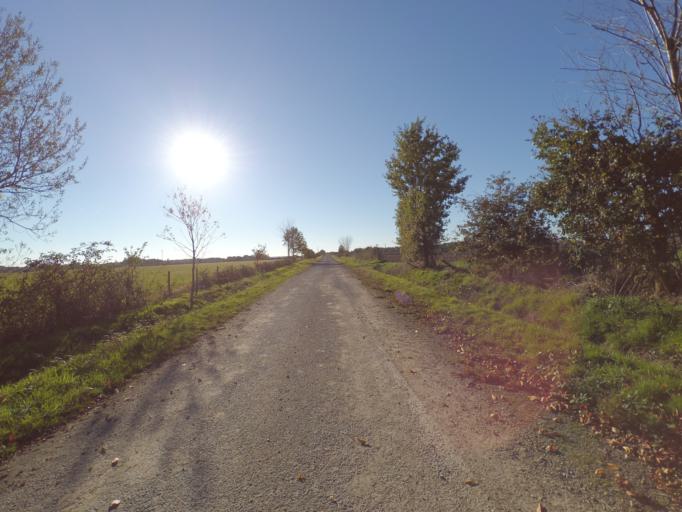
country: FR
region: Pays de la Loire
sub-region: Departement de la Loire-Atlantique
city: Remouille
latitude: 47.0117
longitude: -1.3853
